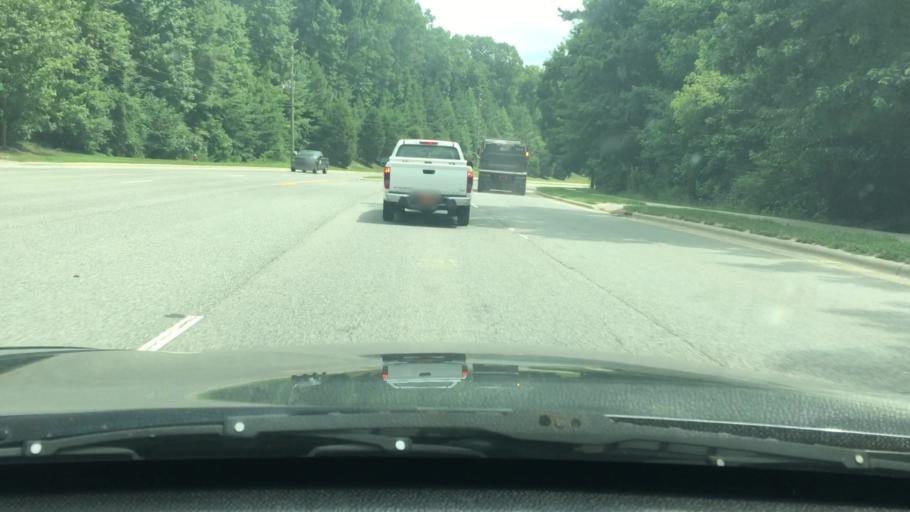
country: US
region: North Carolina
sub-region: Wake County
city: West Raleigh
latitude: 35.8482
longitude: -78.7106
